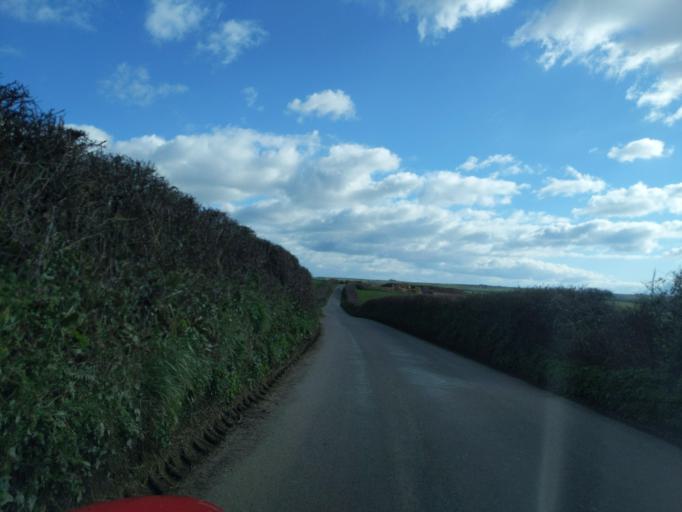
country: GB
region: England
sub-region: Devon
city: Salcombe
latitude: 50.2640
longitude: -3.7187
